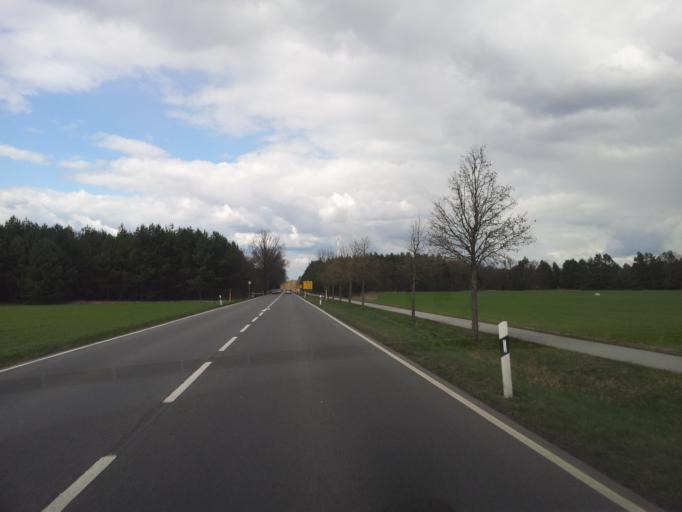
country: DE
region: Saxony
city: Wittichenau
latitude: 51.4055
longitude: 14.2921
